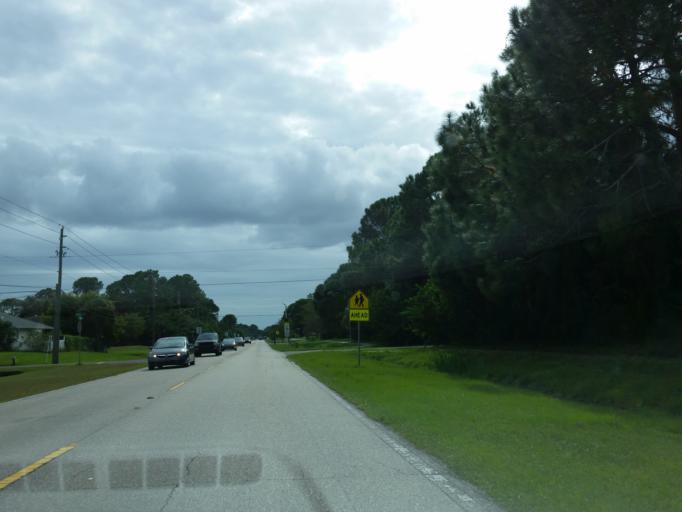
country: US
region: Florida
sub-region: Sarasota County
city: North Port
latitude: 27.0618
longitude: -82.1982
